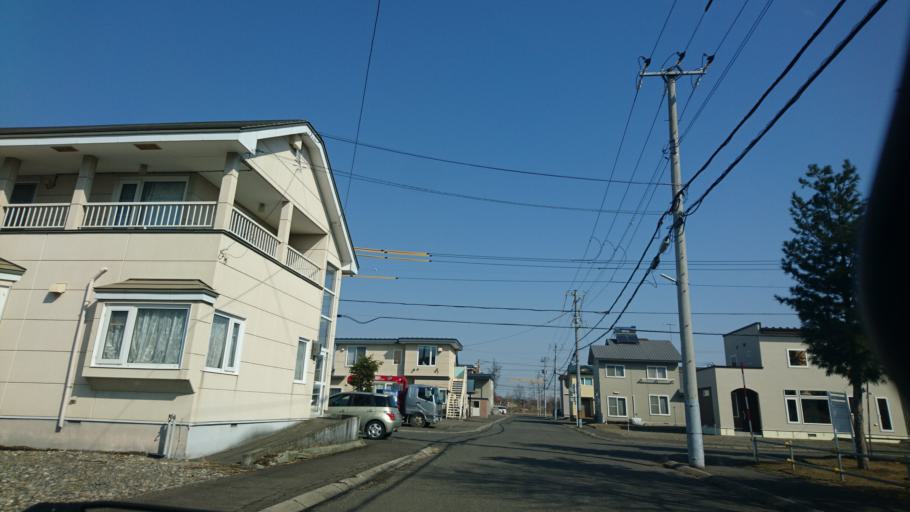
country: JP
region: Hokkaido
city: Obihiro
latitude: 42.9141
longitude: 143.1145
